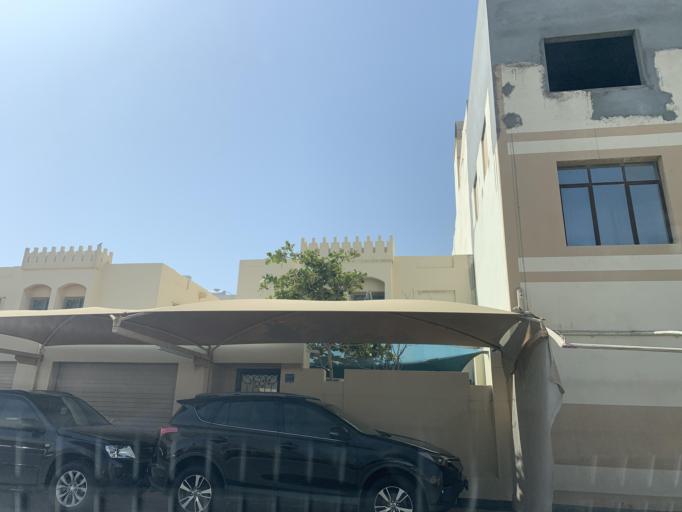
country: BH
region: Muharraq
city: Al Muharraq
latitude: 26.2694
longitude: 50.5966
